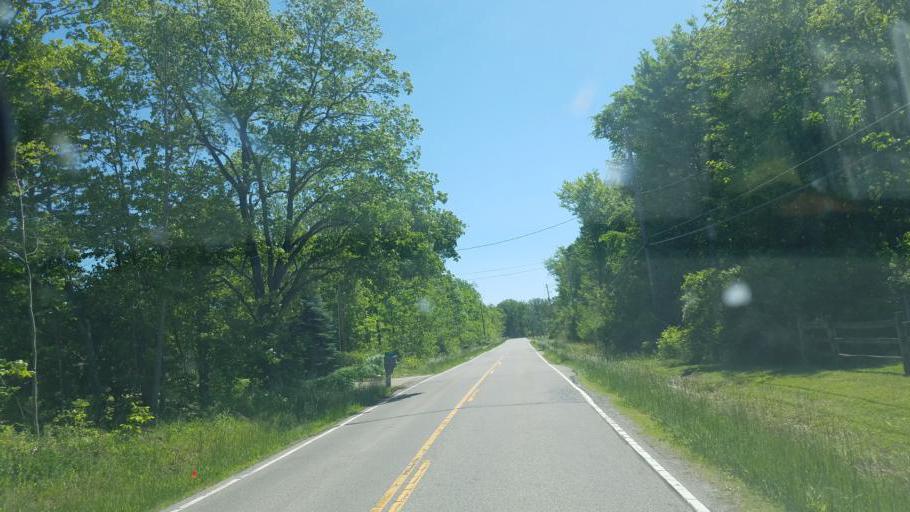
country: US
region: Ohio
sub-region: Geauga County
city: Bainbridge
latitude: 41.3695
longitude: -81.3073
